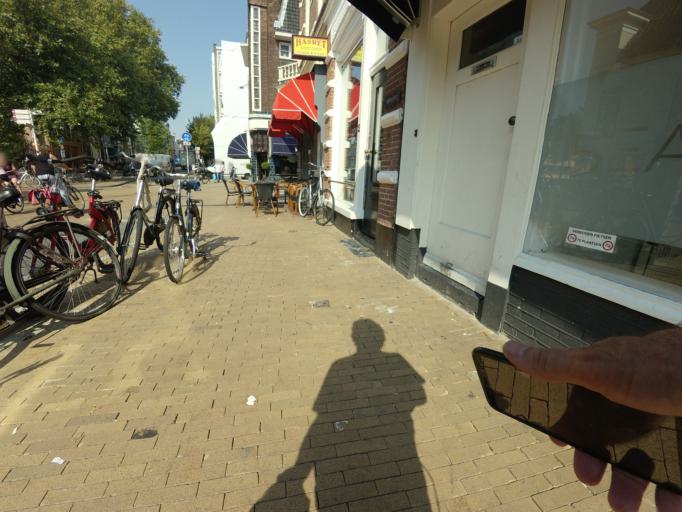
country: NL
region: Groningen
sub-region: Gemeente Groningen
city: Groningen
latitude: 53.2159
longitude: 6.5715
